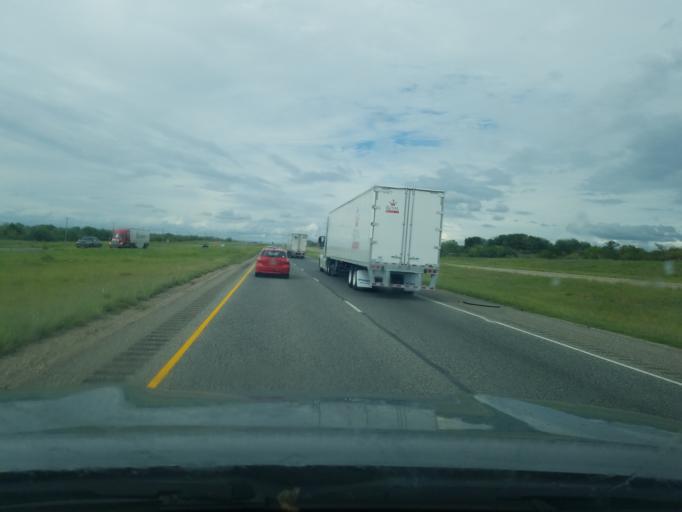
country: US
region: Texas
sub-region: Frio County
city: Pearsall
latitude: 28.9767
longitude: -99.0716
